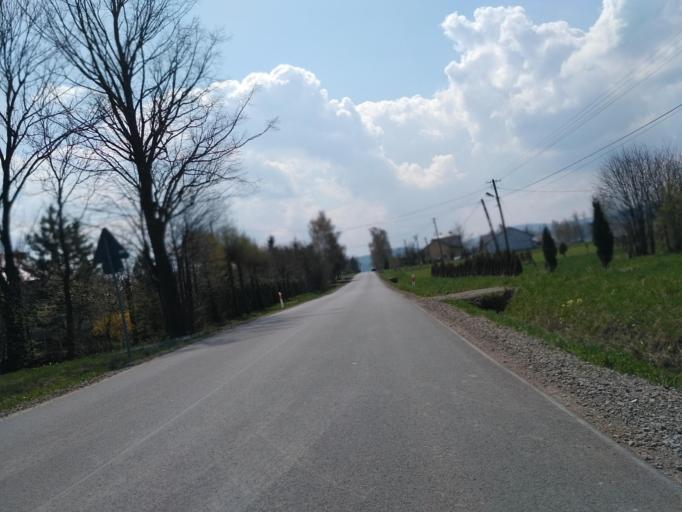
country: PL
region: Subcarpathian Voivodeship
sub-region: Powiat sanocki
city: Zarszyn
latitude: 49.5191
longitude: 21.9998
